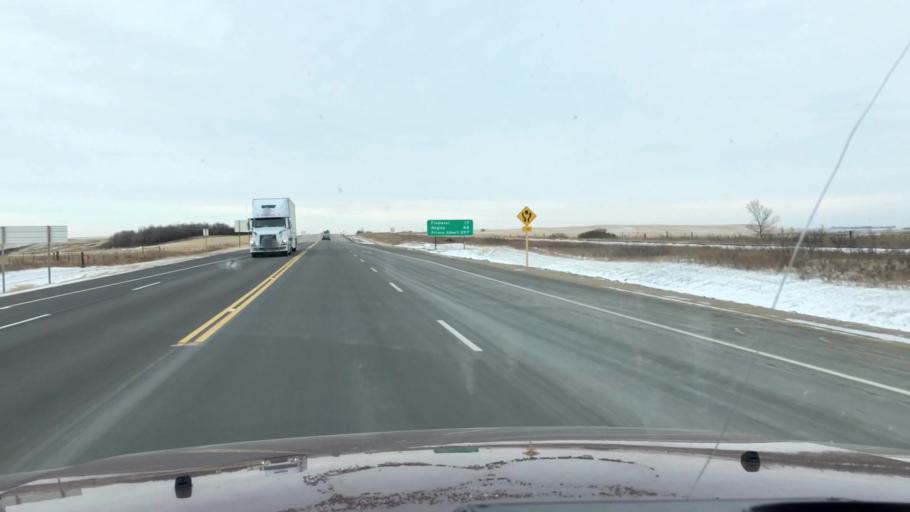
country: CA
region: Saskatchewan
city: Moose Jaw
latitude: 50.8481
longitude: -105.5619
